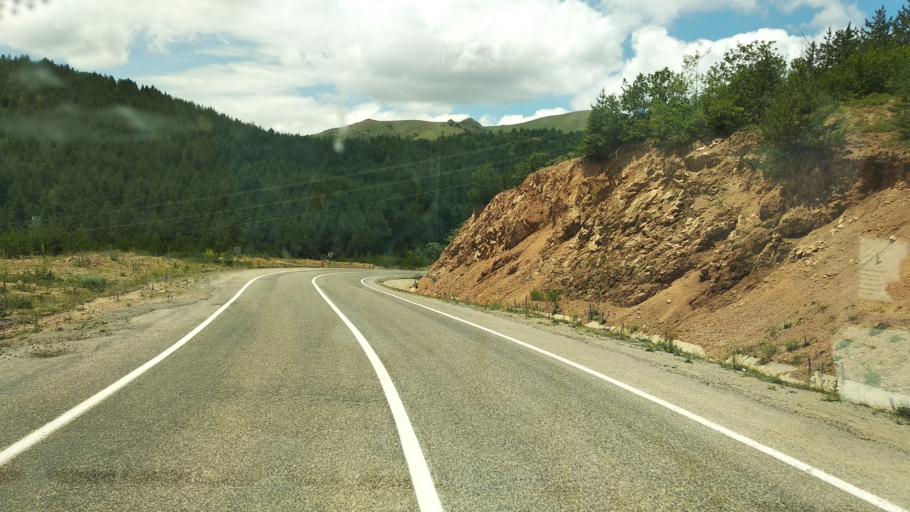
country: TR
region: Gumushane
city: Kose
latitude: 40.2957
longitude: 39.5719
